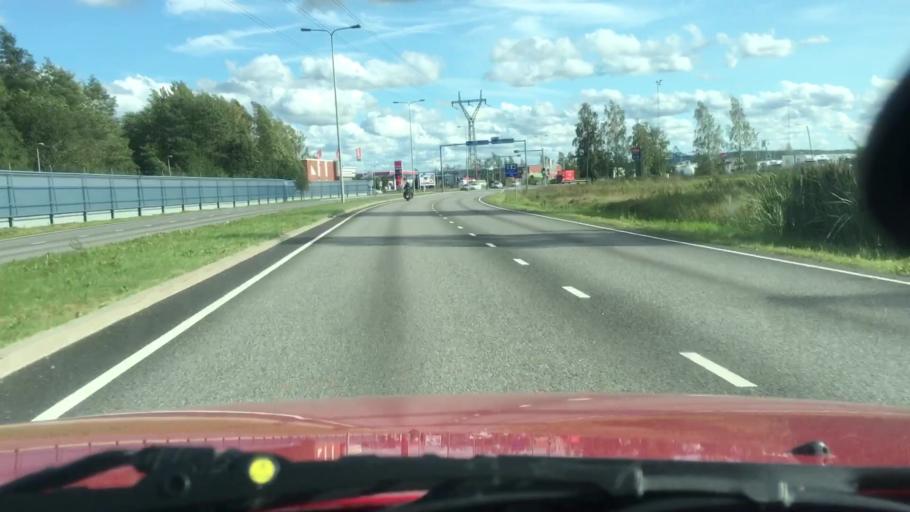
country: FI
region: Varsinais-Suomi
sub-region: Turku
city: Raisio
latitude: 60.4514
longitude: 22.1993
